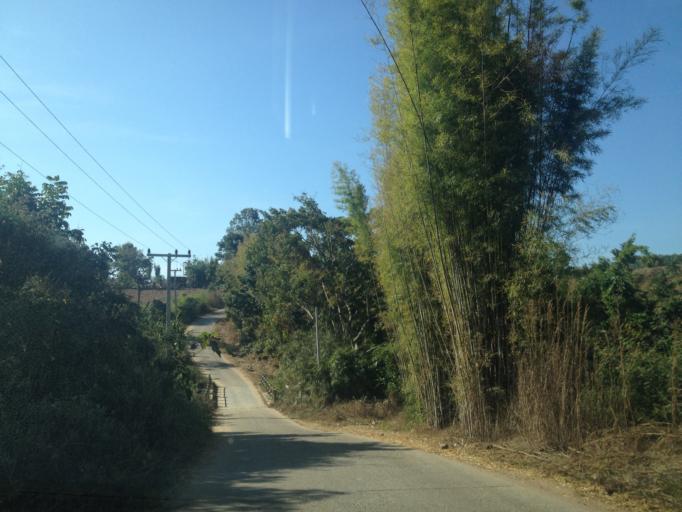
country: TH
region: Mae Hong Son
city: Ban Huai I Huak
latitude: 18.0757
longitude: 98.1871
